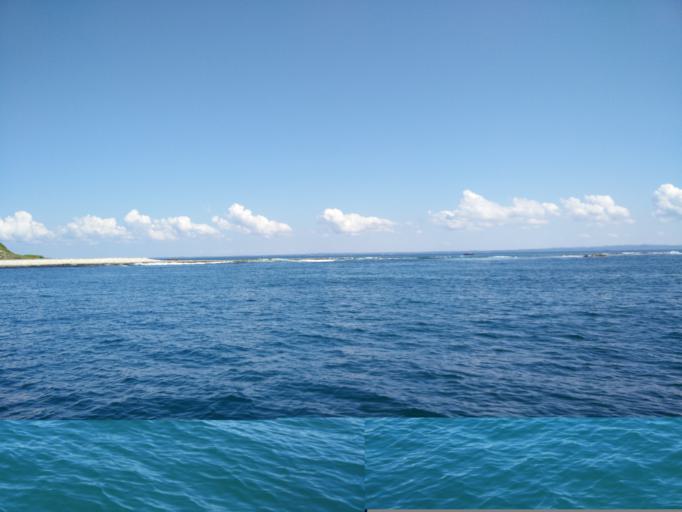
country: MM
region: Ayeyarwady
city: Pathein
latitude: 16.8846
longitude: 94.2697
